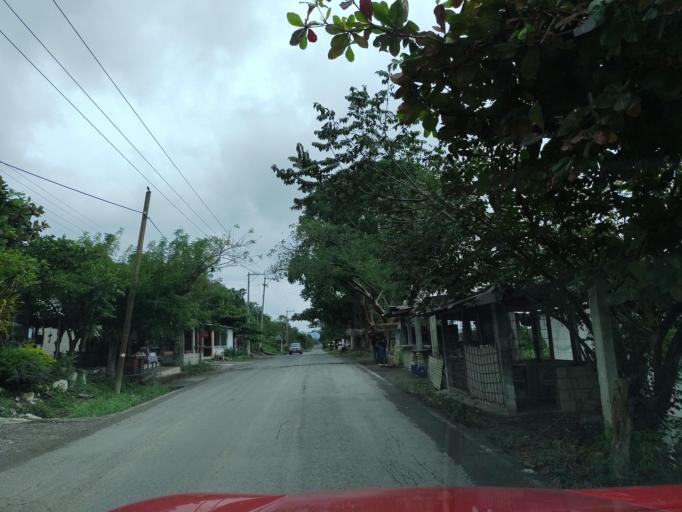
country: MX
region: Puebla
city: Espinal
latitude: 20.2630
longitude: -97.3534
